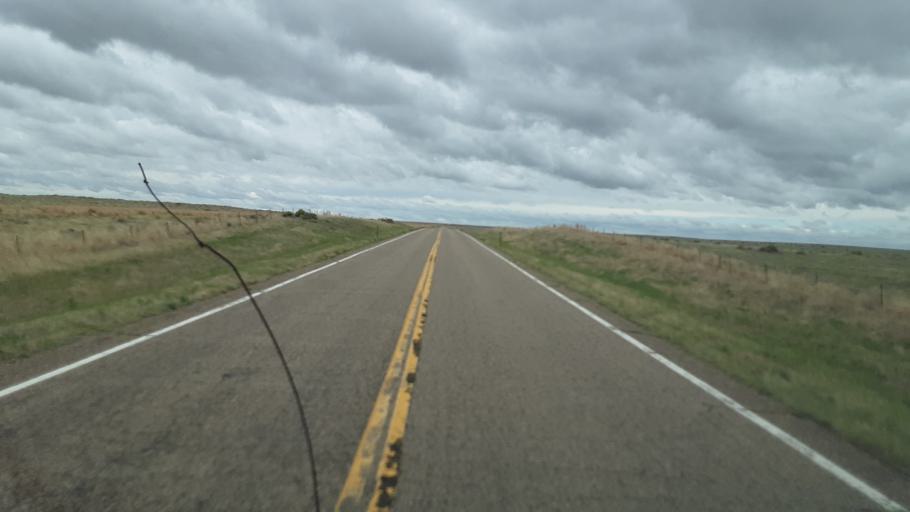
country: US
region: Colorado
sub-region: Lincoln County
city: Hugo
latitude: 38.8509
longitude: -103.5856
